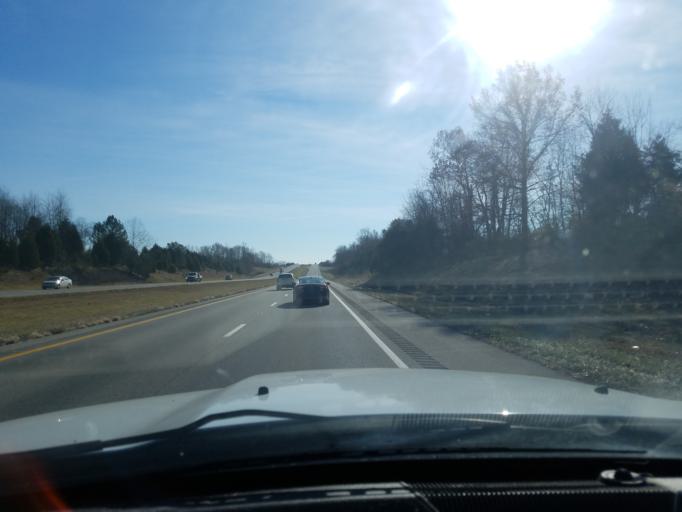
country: US
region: Ohio
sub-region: Adams County
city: Winchester
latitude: 38.9447
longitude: -83.6762
